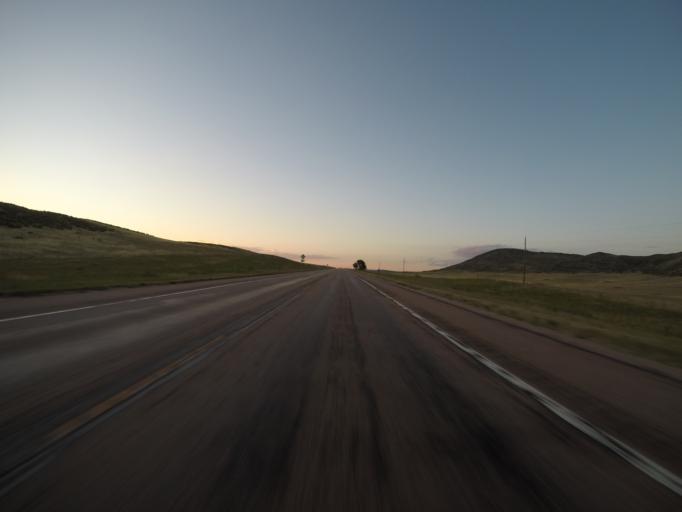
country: US
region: Colorado
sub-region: Larimer County
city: Laporte
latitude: 40.7424
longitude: -105.1706
